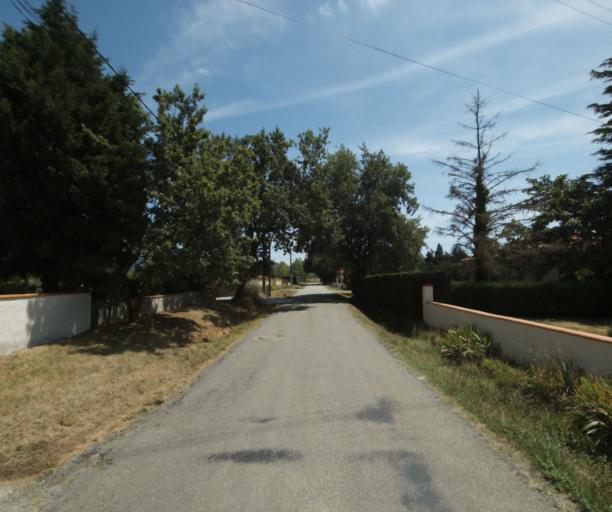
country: FR
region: Midi-Pyrenees
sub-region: Departement de la Haute-Garonne
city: Revel
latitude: 43.4867
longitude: 2.0269
